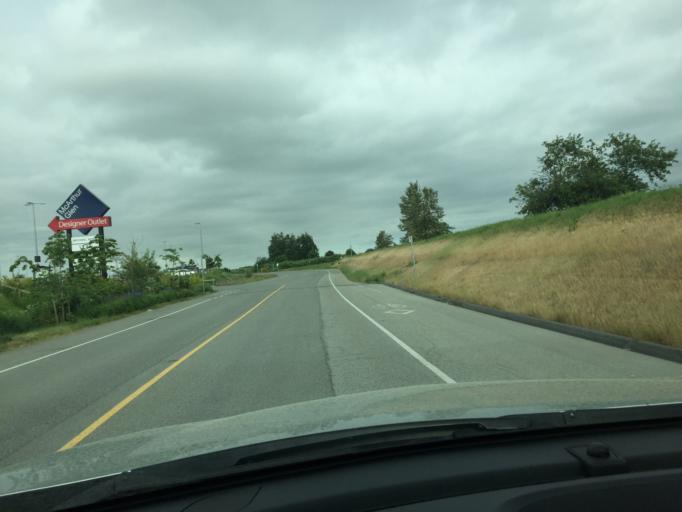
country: CA
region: British Columbia
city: Richmond
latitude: 49.1988
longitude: -123.1402
